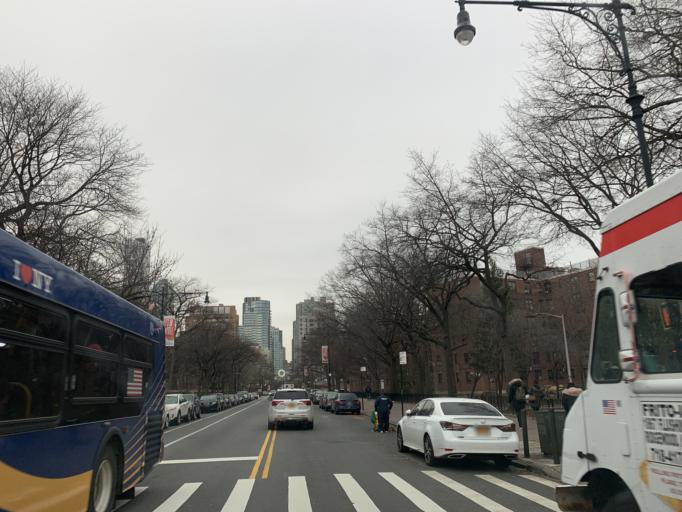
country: US
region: New York
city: New York City
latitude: 40.6934
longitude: -73.9753
